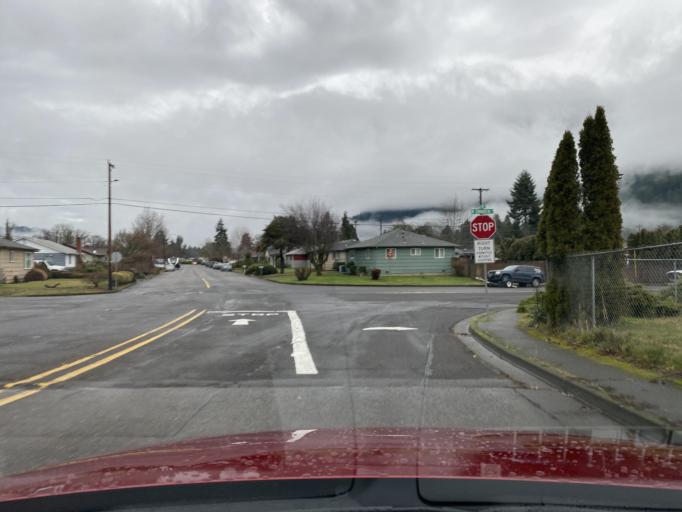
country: US
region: Oregon
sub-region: Lane County
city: Oakridge
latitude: 43.7507
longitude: -122.4815
